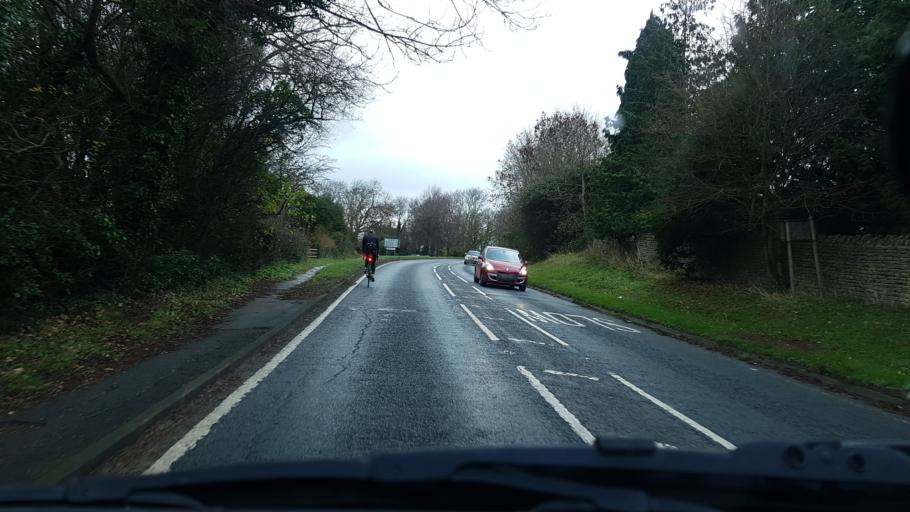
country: GB
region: England
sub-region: Gloucestershire
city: Gotherington
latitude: 51.9310
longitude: -2.0398
